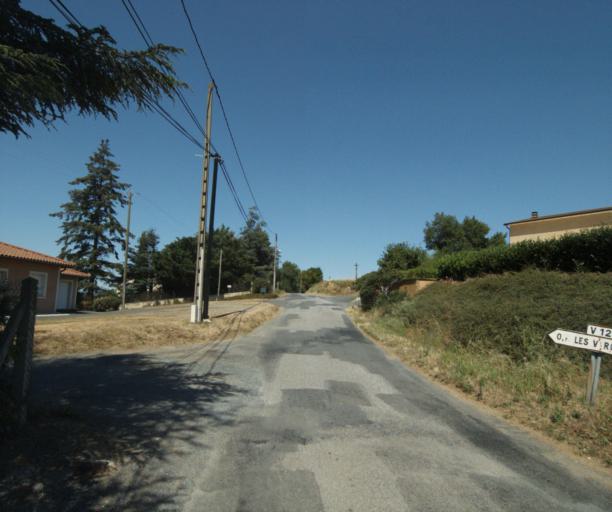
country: FR
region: Rhone-Alpes
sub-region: Departement du Rhone
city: Courzieu
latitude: 45.7506
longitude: 4.5806
